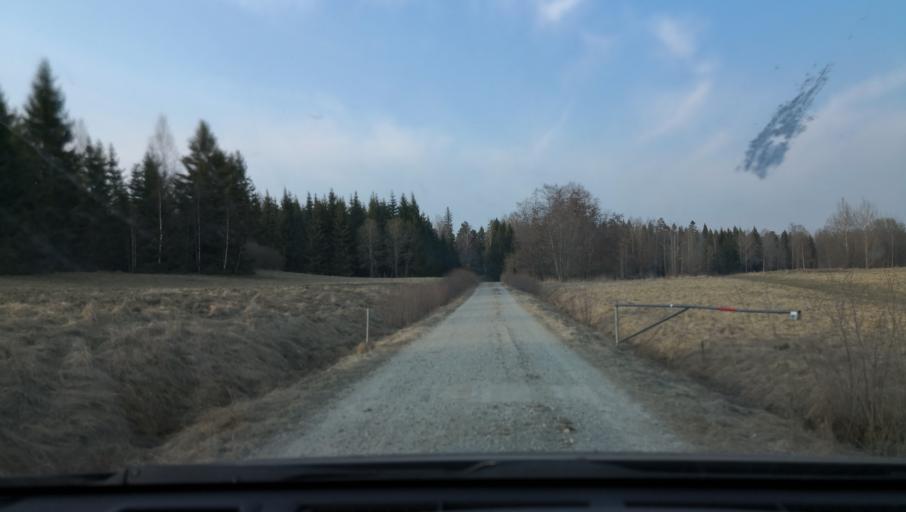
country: SE
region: OErebro
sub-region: Orebro Kommun
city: Hovsta
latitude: 59.3906
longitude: 15.2703
